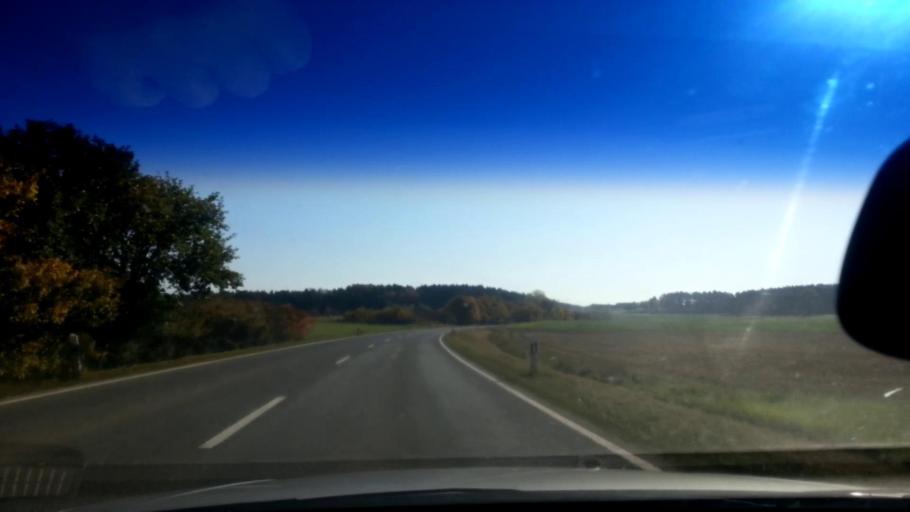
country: DE
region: Bavaria
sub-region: Upper Franconia
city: Stadelhofen
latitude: 49.9953
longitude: 11.2186
